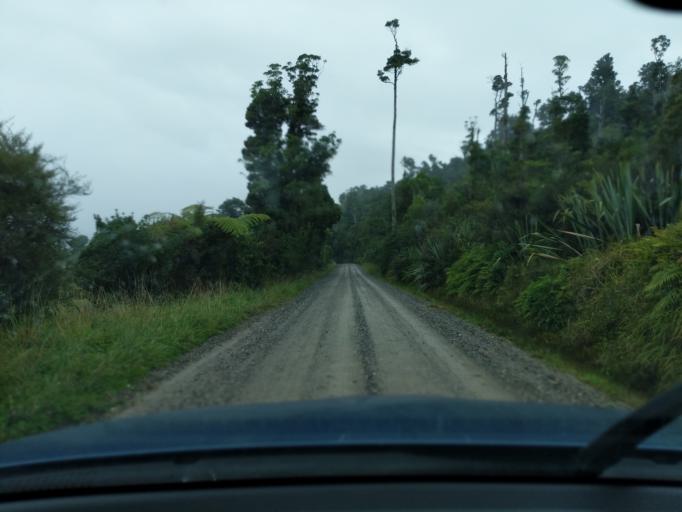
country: NZ
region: Tasman
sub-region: Tasman District
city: Takaka
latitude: -40.6470
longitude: 172.4715
